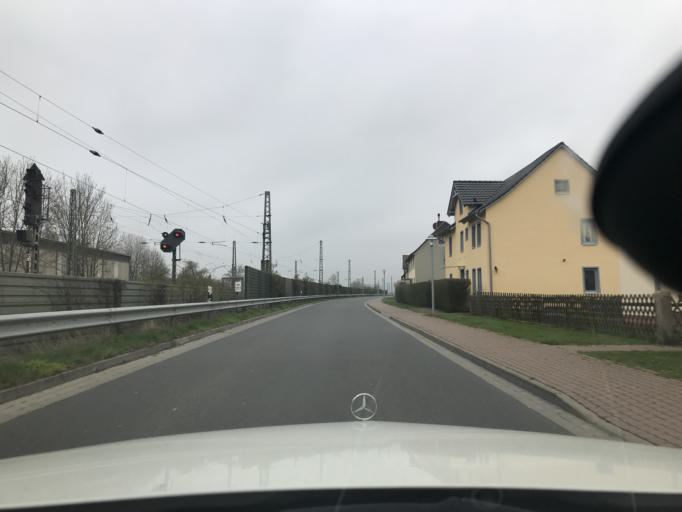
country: DE
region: Lower Saxony
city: Gemeinde Friedland
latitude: 51.4586
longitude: 9.9203
